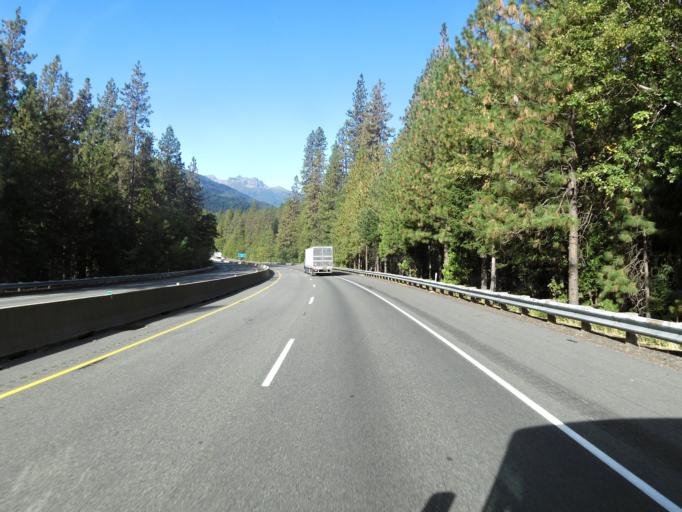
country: US
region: California
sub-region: Siskiyou County
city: Dunsmuir
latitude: 41.1517
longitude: -122.3061
